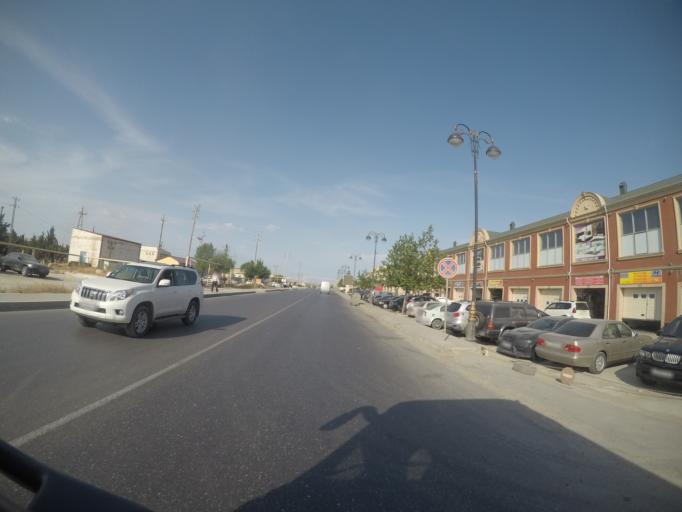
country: AZ
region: Baki
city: Bilajari
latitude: 40.4435
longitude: 49.7892
